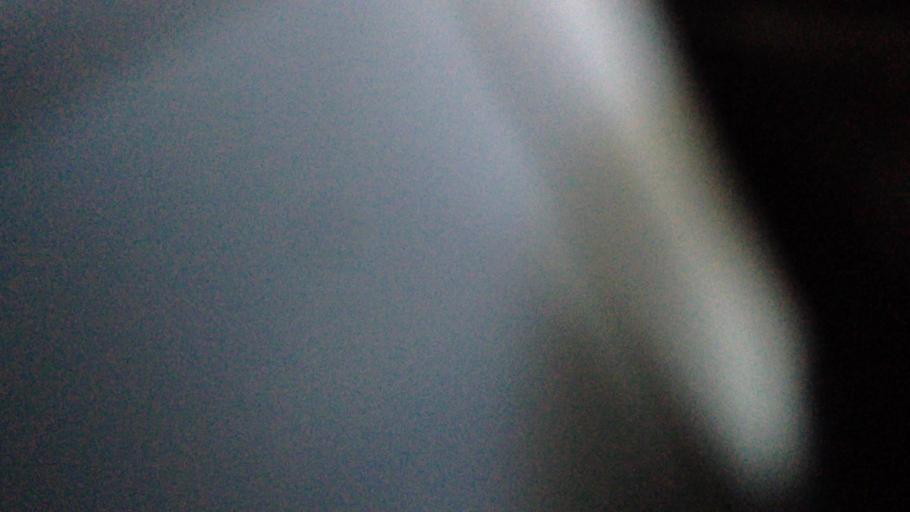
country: US
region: New York
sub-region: Columbia County
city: Hudson
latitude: 42.2530
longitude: -73.7878
